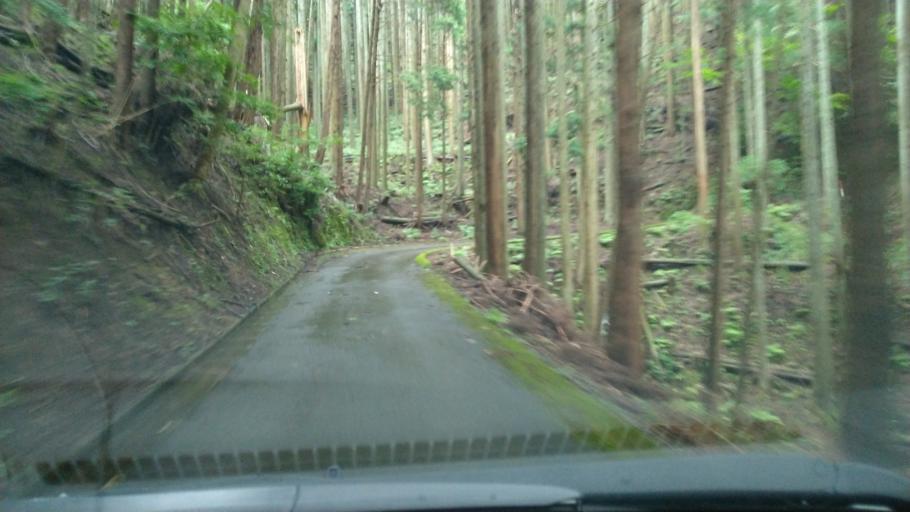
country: JP
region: Kyoto
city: Ayabe
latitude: 35.2281
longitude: 135.2766
